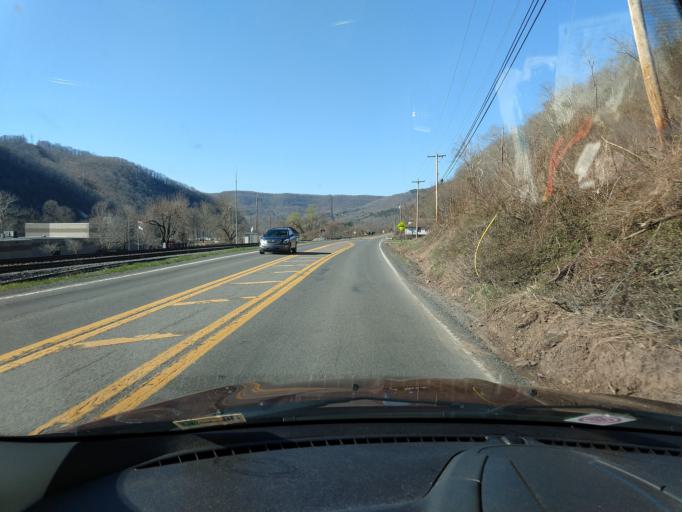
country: US
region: West Virginia
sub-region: Summers County
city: Hinton
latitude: 37.7067
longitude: -80.8872
